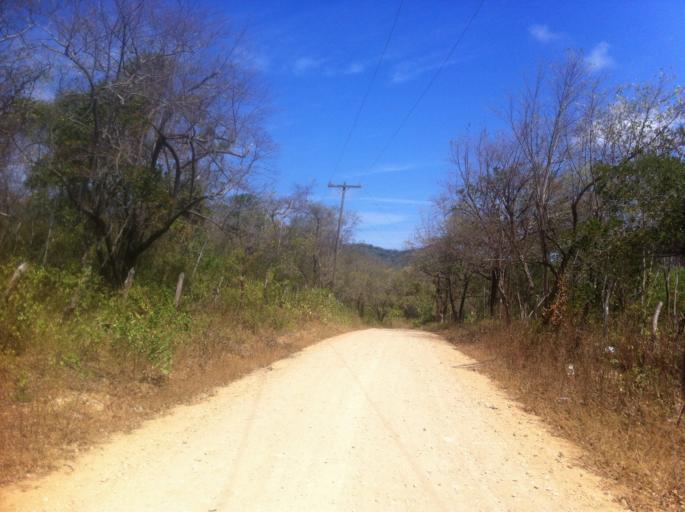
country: NI
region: Rivas
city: Tola
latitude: 11.4083
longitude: -86.0113
